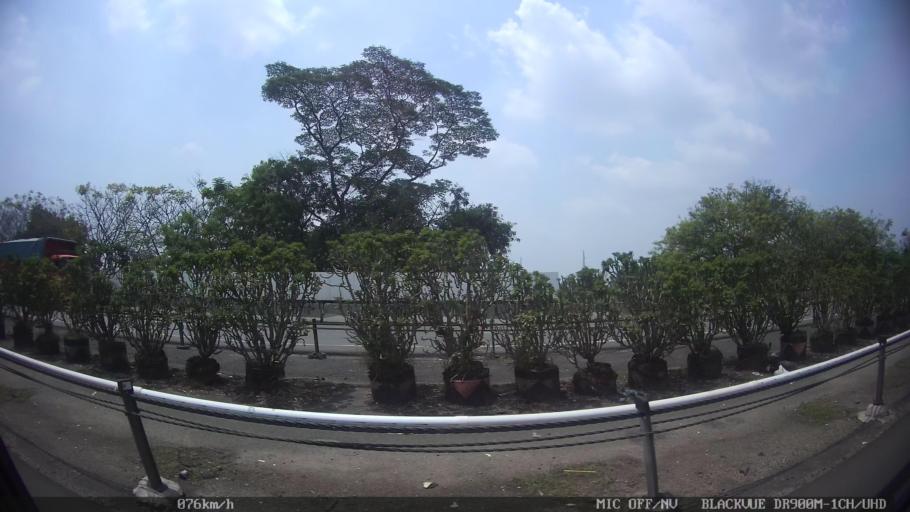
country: ID
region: West Java
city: Kresek
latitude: -6.1407
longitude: 106.2667
